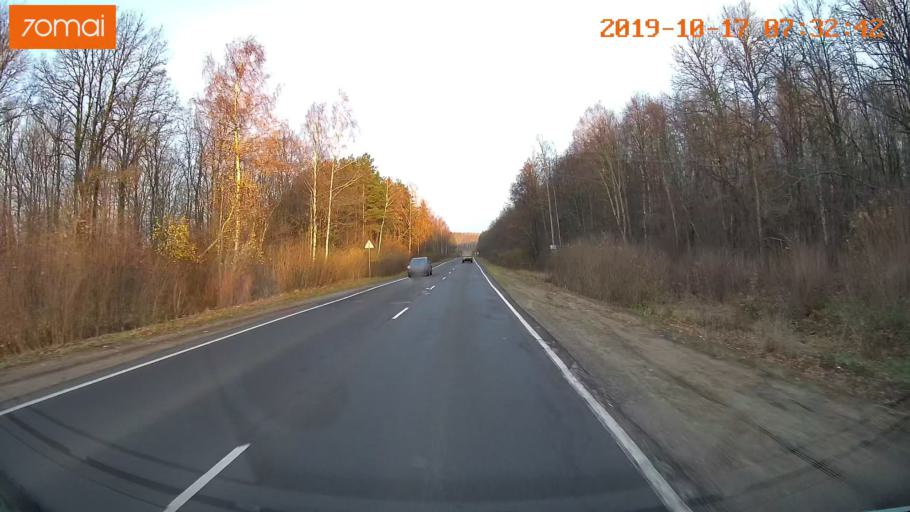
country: RU
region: Ivanovo
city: Gavrilov Posad
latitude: 56.3987
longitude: 39.9692
